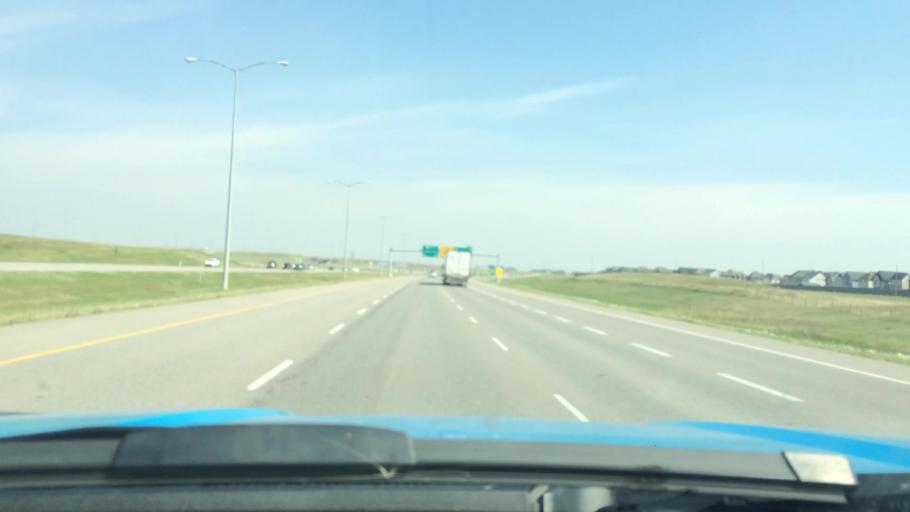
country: CA
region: Alberta
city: Chestermere
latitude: 50.9067
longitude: -113.9284
